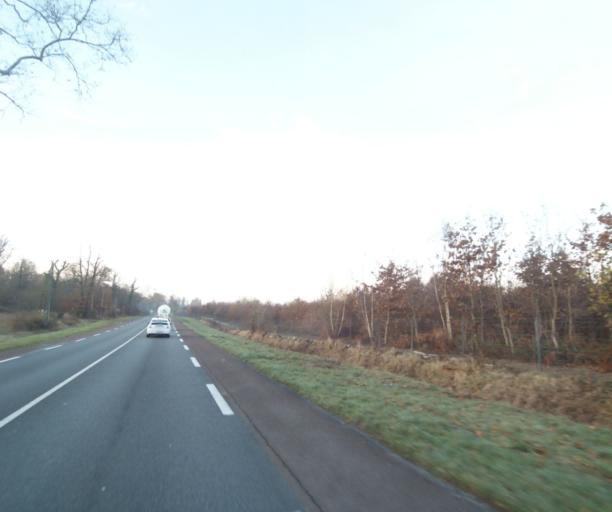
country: FR
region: Poitou-Charentes
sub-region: Departement de la Charente-Maritime
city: Fontcouverte
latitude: 45.7594
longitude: -0.5897
